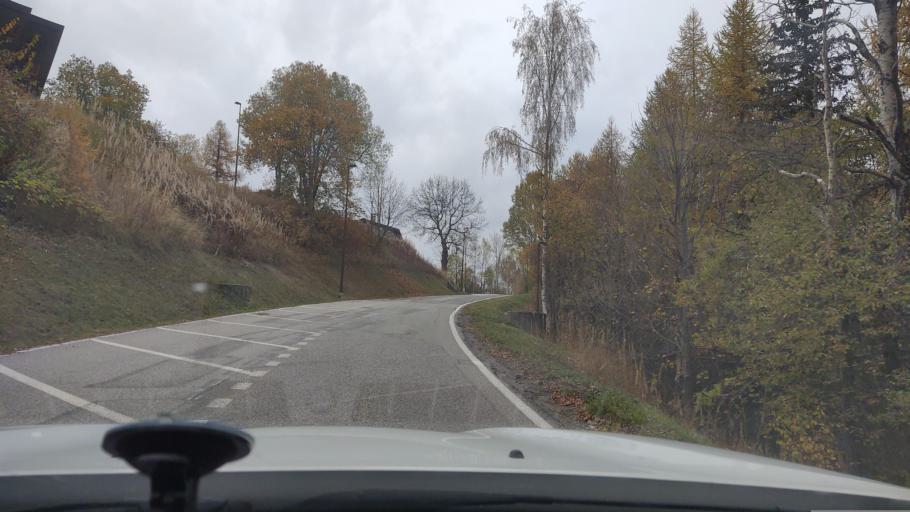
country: FR
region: Rhone-Alpes
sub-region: Departement de la Savoie
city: Seez
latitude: 45.5954
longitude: 6.7914
